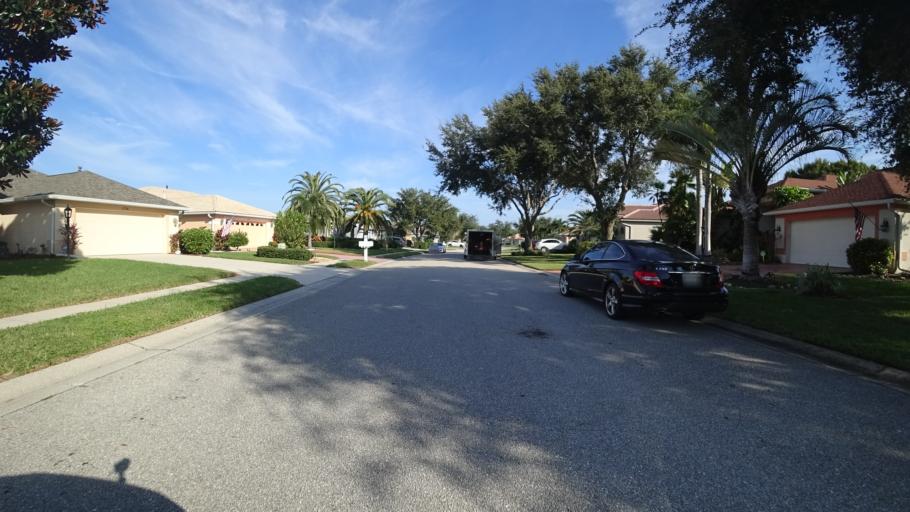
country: US
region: Florida
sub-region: Sarasota County
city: Desoto Lakes
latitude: 27.4204
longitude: -82.4981
